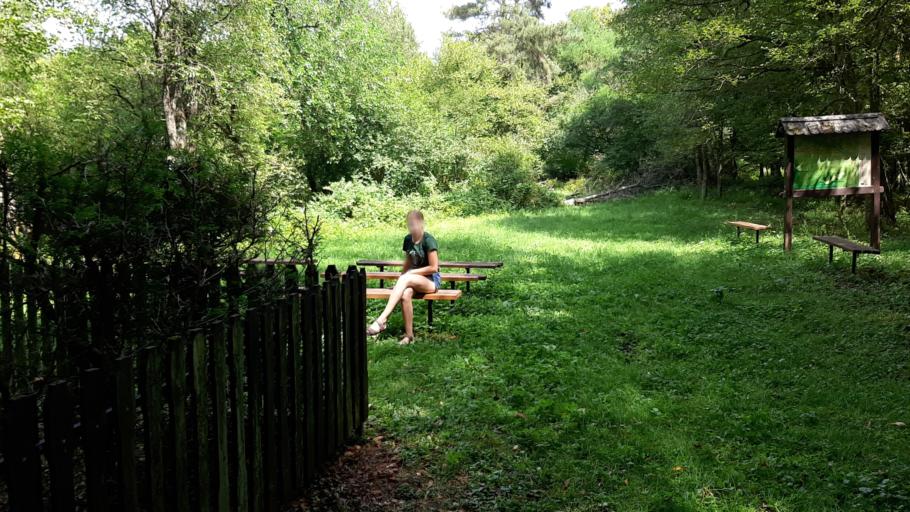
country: HU
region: Vas
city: Szentgotthard
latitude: 46.9406
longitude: 16.3568
